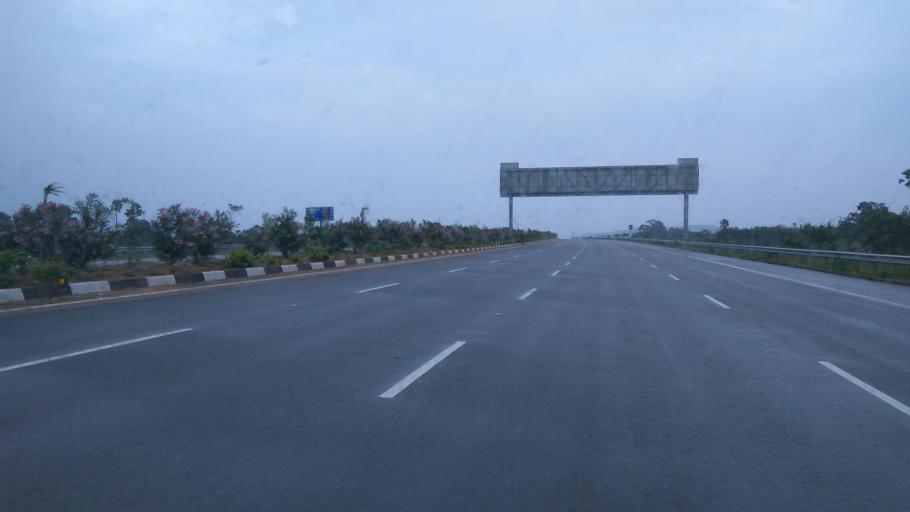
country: IN
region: Telangana
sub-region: Rangareddi
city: Ghatkesar
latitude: 17.4606
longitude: 78.6701
